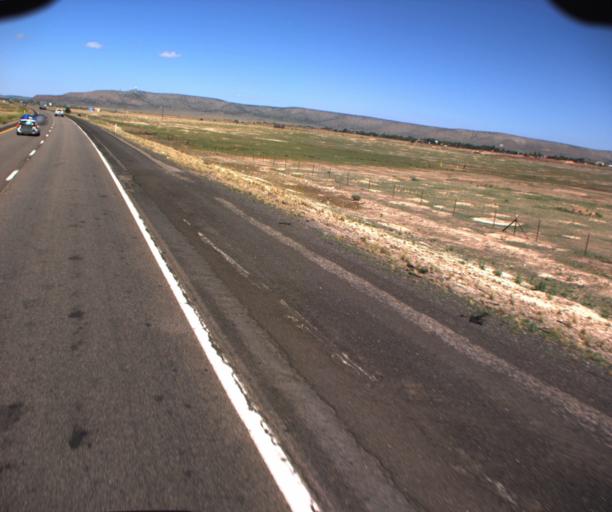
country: US
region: Arizona
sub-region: Yavapai County
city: Paulden
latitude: 35.3142
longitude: -112.8635
